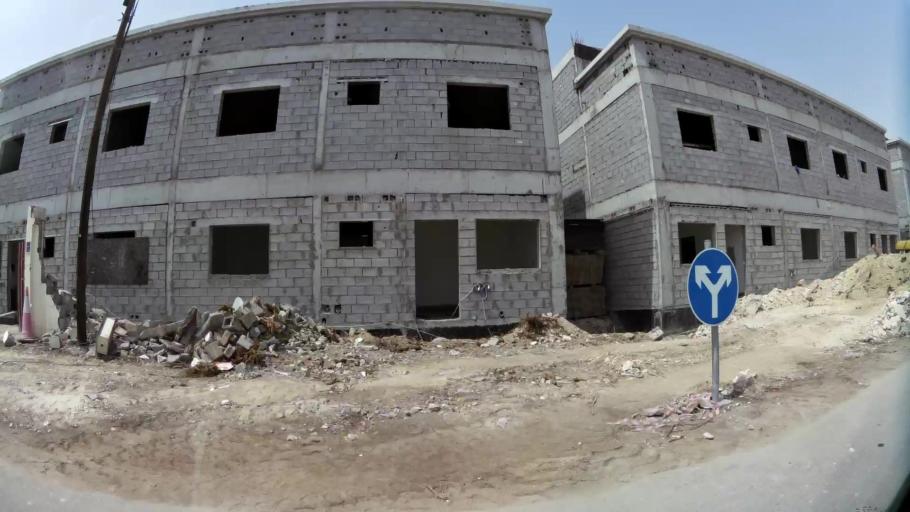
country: QA
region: Baladiyat ar Rayyan
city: Ar Rayyan
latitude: 25.2452
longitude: 51.4223
